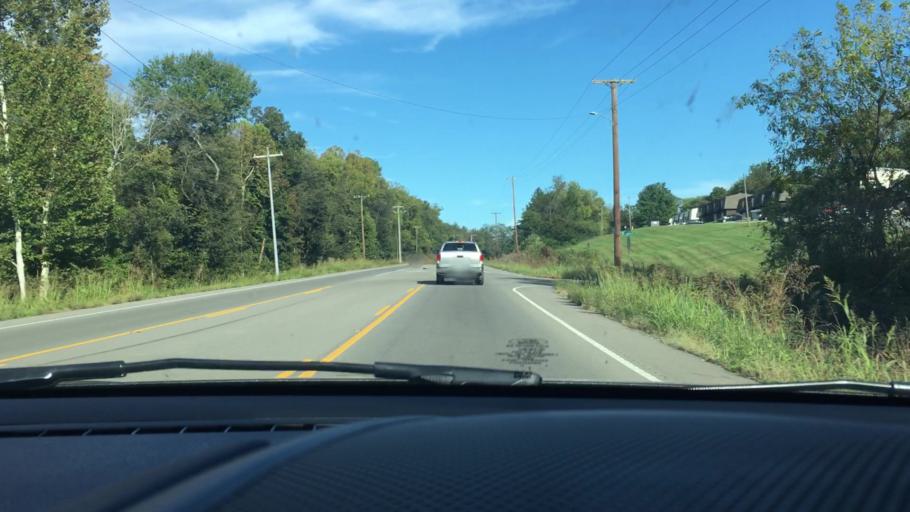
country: US
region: Tennessee
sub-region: Montgomery County
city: Clarksville
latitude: 36.5014
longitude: -87.3037
